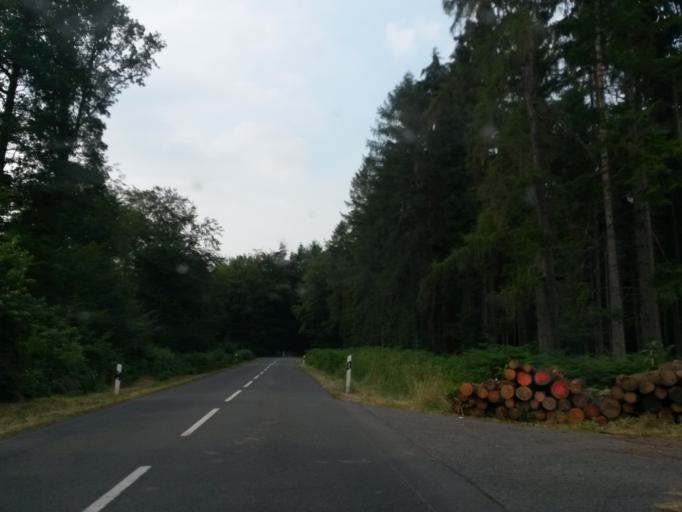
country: DE
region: North Rhine-Westphalia
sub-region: Regierungsbezirk Koln
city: Hennef
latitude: 50.7867
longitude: 7.3019
